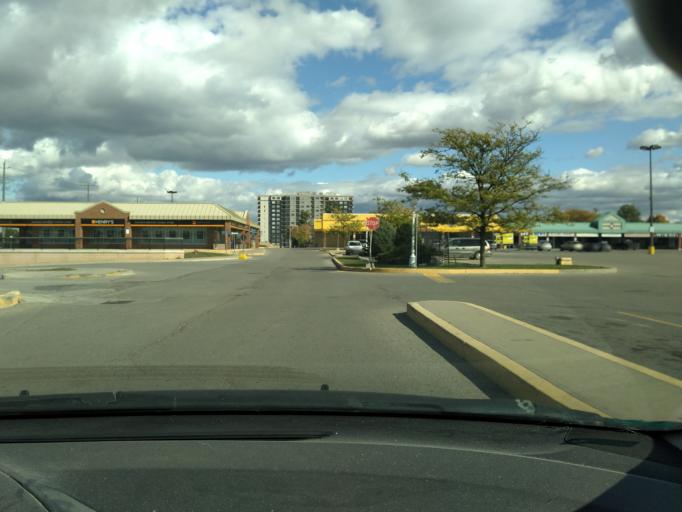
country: CA
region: Ontario
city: Newmarket
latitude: 44.0551
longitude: -79.4745
